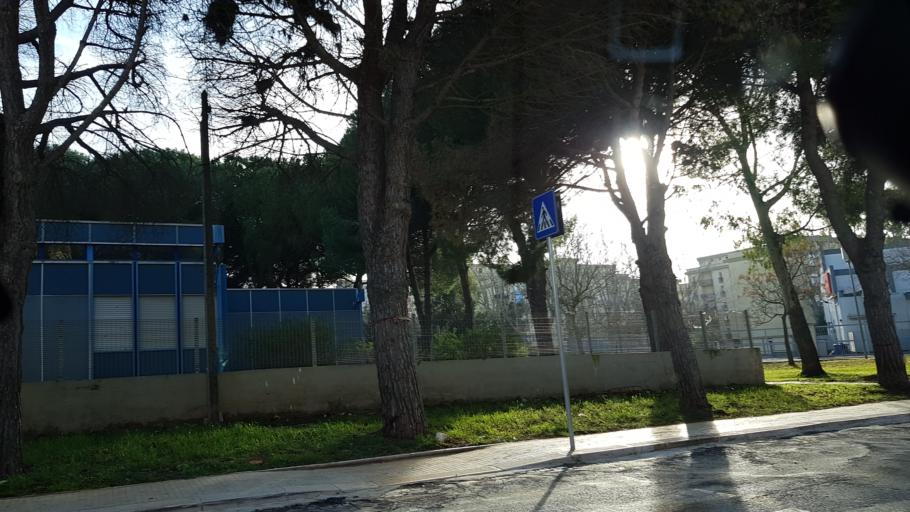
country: IT
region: Apulia
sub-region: Provincia di Brindisi
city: Brindisi
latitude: 40.6206
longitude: 17.9163
